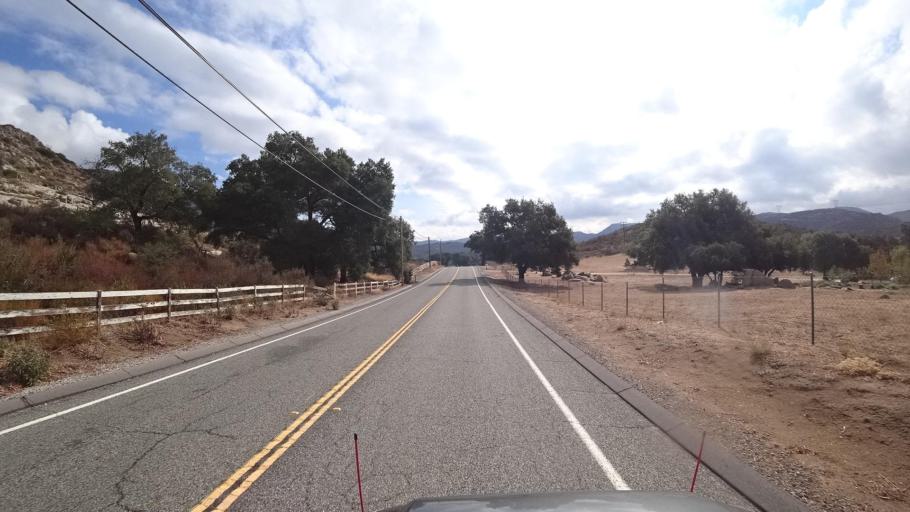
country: MX
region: Baja California
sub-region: Tecate
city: Hacienda Tecate
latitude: 32.5957
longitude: -116.5340
